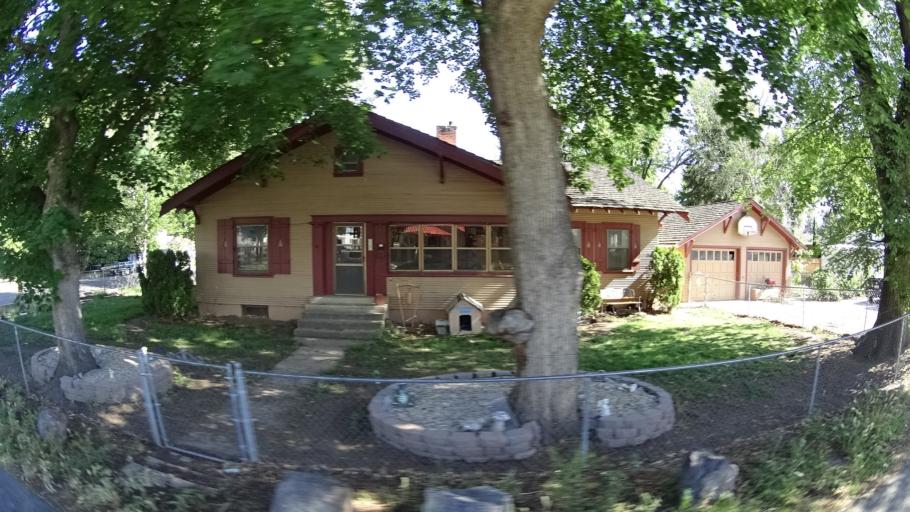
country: US
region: Idaho
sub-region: Ada County
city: Garden City
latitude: 43.6203
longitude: -116.2456
